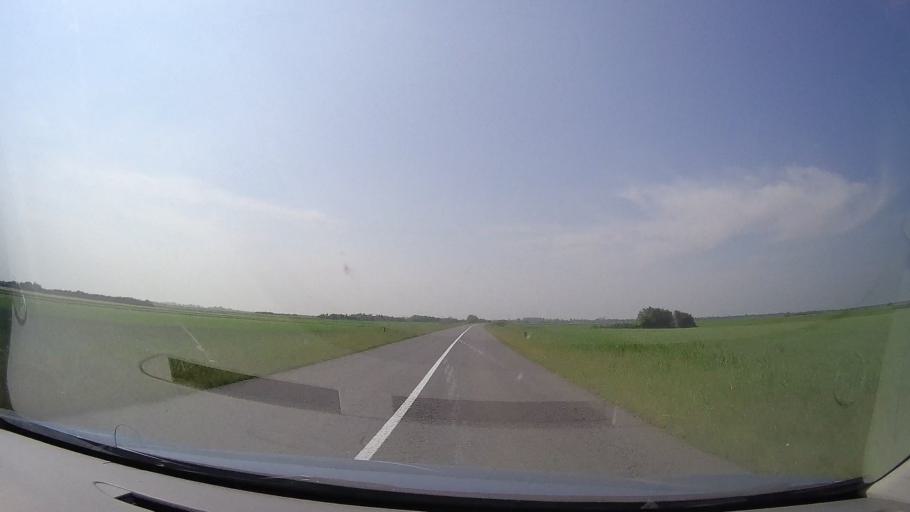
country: RS
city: Jarkovac
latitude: 45.2934
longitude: 20.7642
